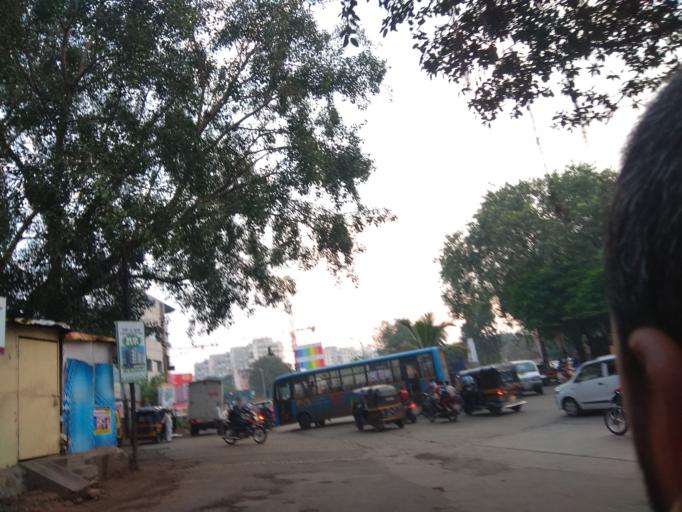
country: IN
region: Maharashtra
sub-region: Pune Division
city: Kharakvasla
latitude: 18.4836
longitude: 73.8095
